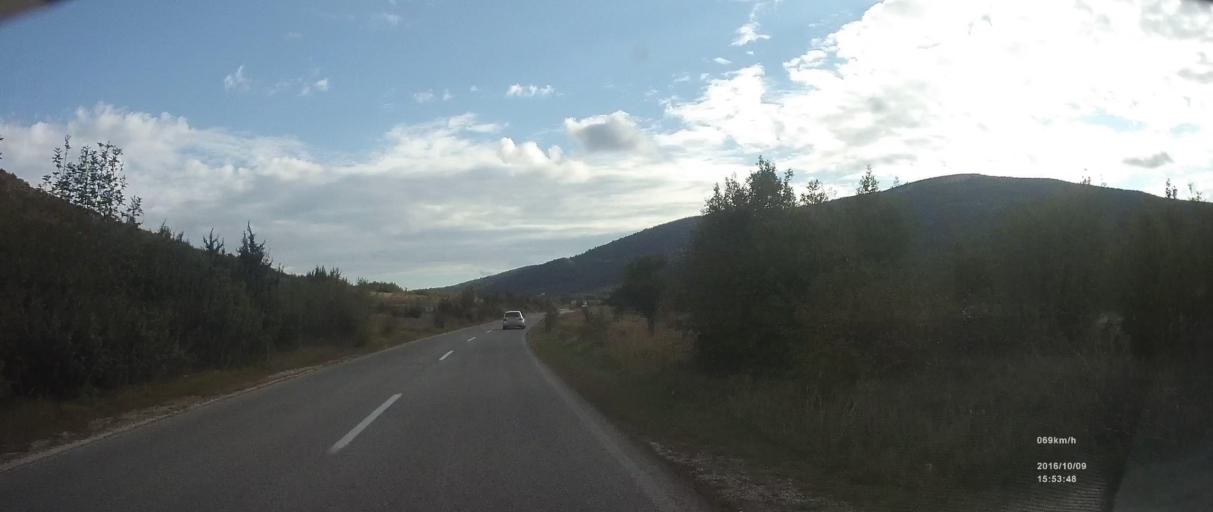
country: HR
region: Splitsko-Dalmatinska
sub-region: Grad Trogir
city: Trogir
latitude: 43.6018
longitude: 16.2248
